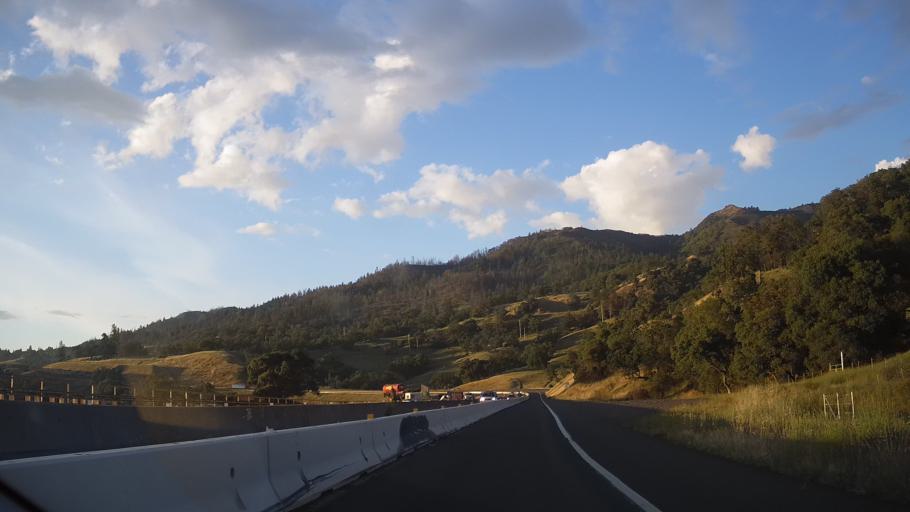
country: US
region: California
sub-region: Mendocino County
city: Redwood Valley
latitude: 39.3085
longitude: -123.2999
